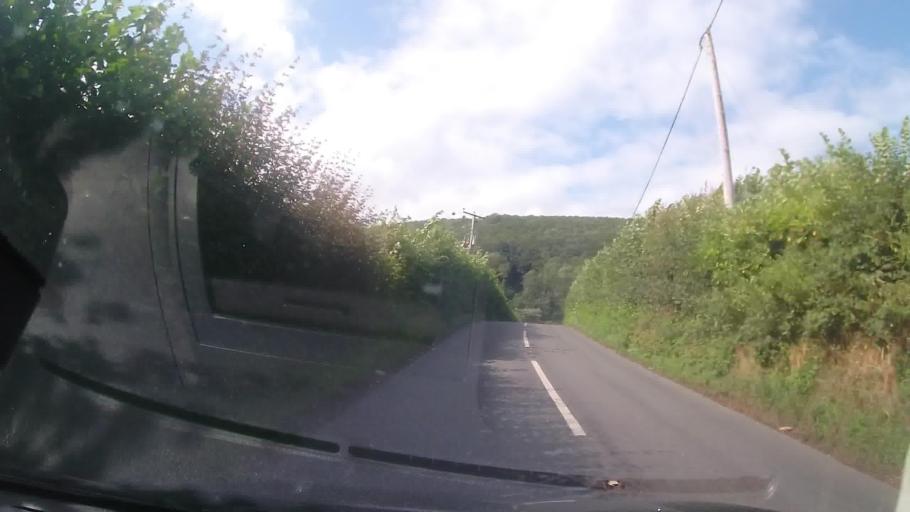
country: GB
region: Wales
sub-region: Sir Powys
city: Knighton
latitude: 52.3495
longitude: -3.0269
